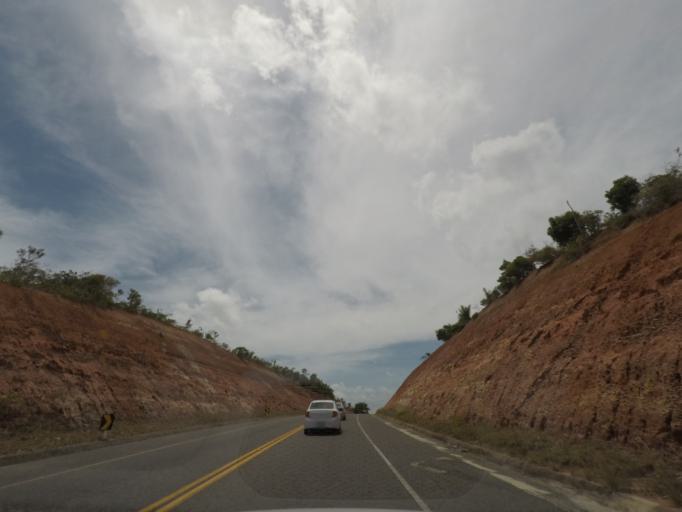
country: BR
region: Bahia
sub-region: Conde
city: Conde
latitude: -11.9107
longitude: -37.6576
